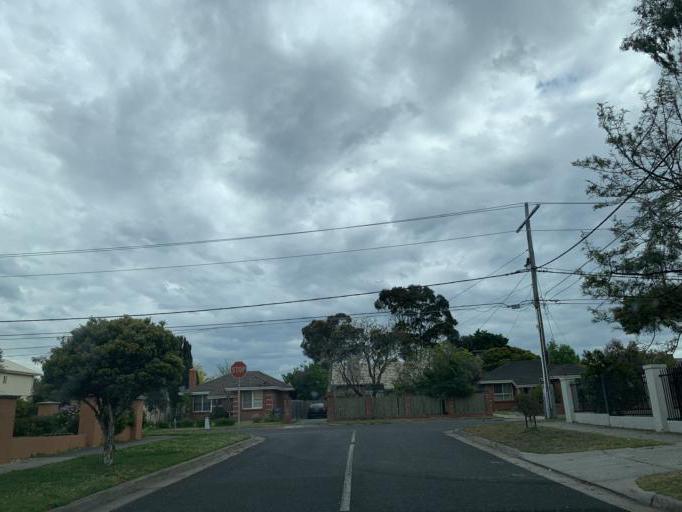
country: AU
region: Victoria
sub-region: Bayside
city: Hampton East
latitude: -37.9350
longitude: 145.0222
